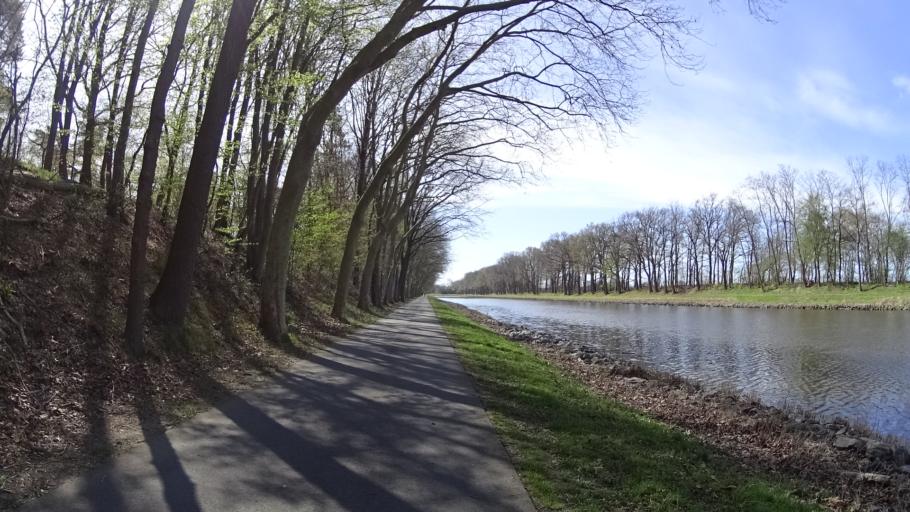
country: DE
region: Lower Saxony
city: Lingen
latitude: 52.5483
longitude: 7.2940
